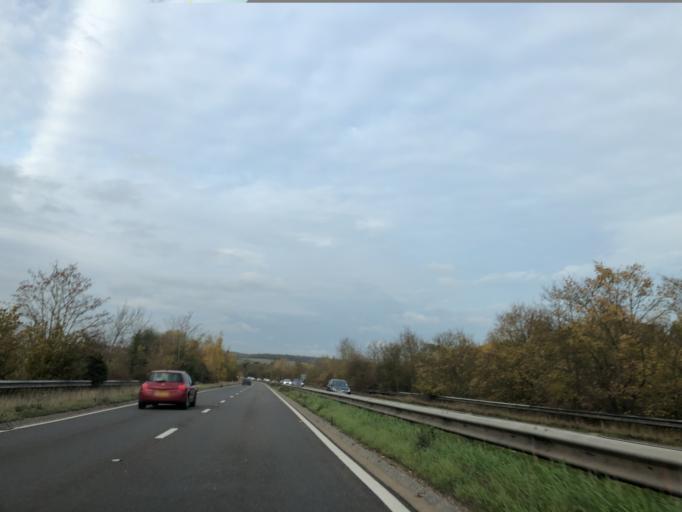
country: GB
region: England
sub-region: Buckinghamshire
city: Marlow
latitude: 51.5710
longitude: -0.7590
